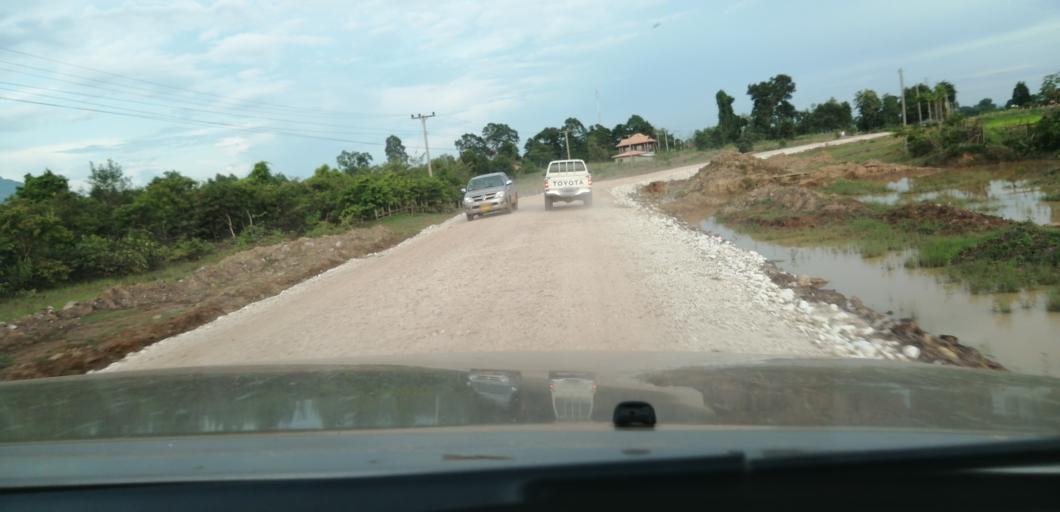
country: LA
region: Attapu
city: Attapu
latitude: 14.7091
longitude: 106.4910
